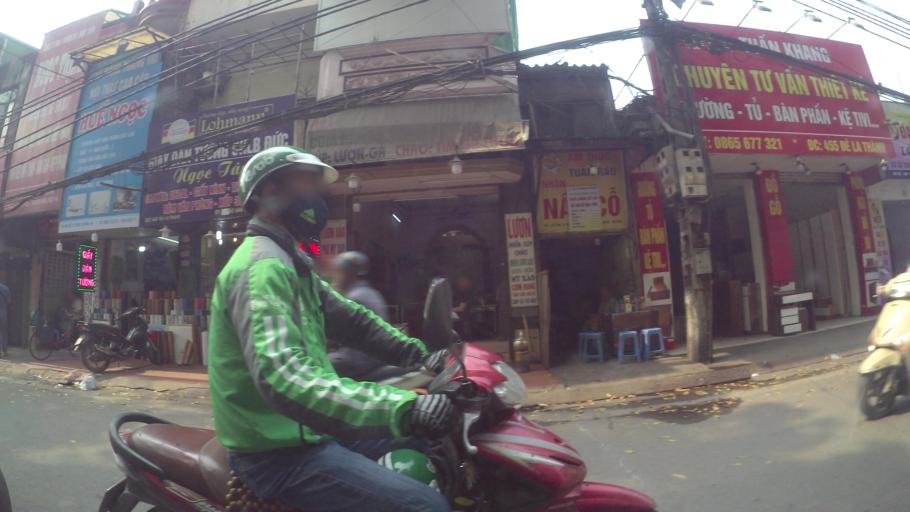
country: VN
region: Ha Noi
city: Dong Da
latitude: 21.0228
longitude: 105.8184
